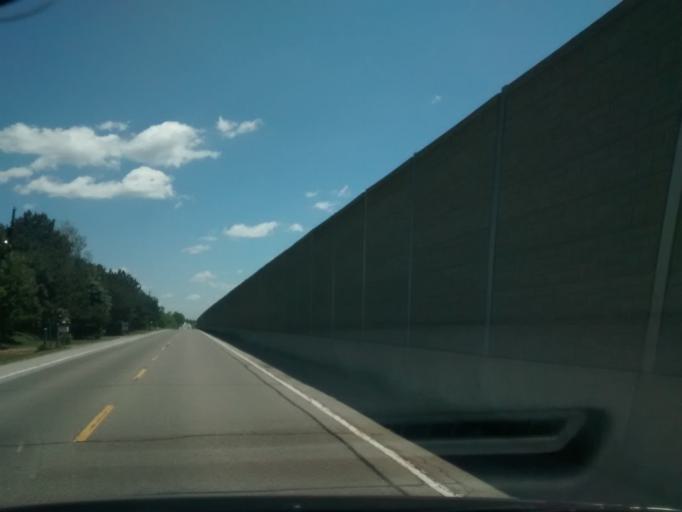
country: CA
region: Ontario
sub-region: Regional Municipality of Niagara
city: St. Catharines
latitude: 43.1798
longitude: -79.3472
